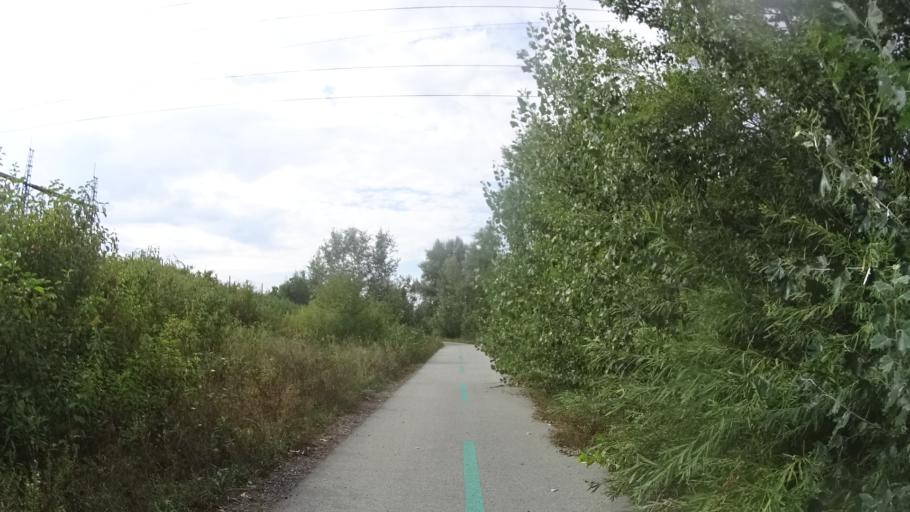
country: SK
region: Trnavsky
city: Gabcikovo
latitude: 47.8851
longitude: 17.5418
